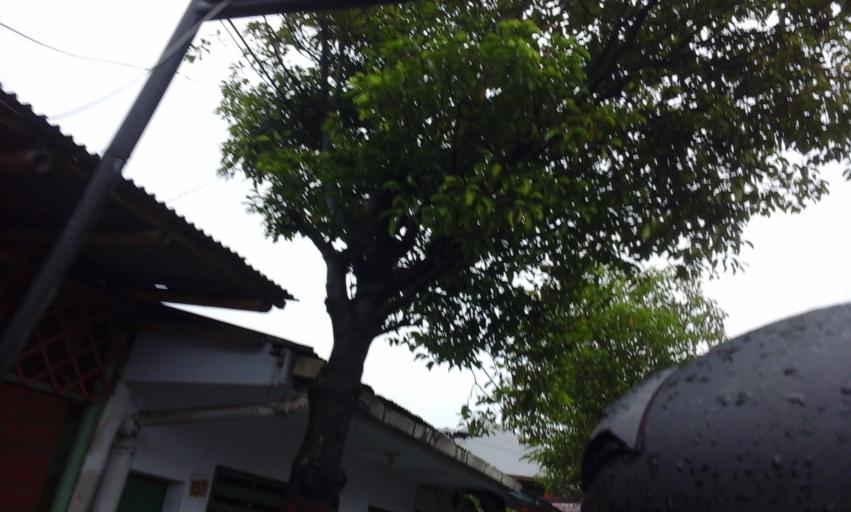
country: ID
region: East Java
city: Lumajang
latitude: -8.1263
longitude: 113.2224
